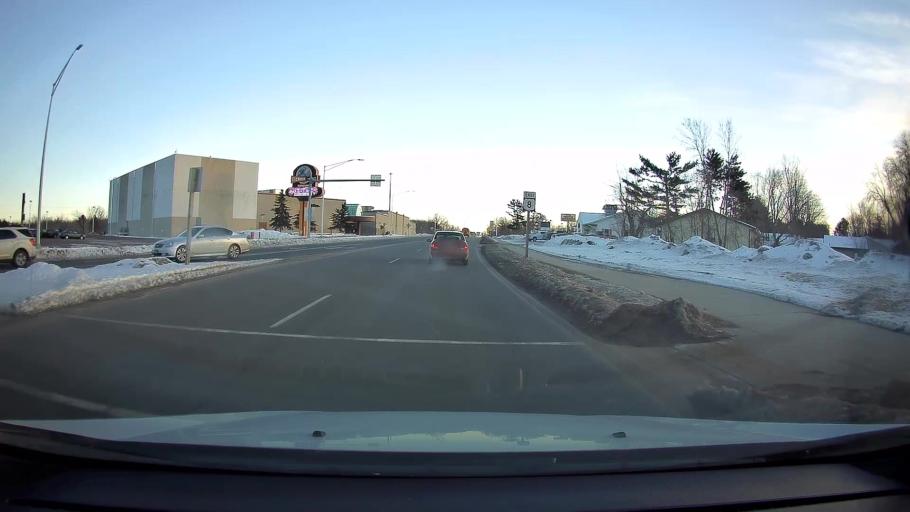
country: US
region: Wisconsin
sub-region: Barron County
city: Turtle Lake
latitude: 45.3960
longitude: -92.1511
